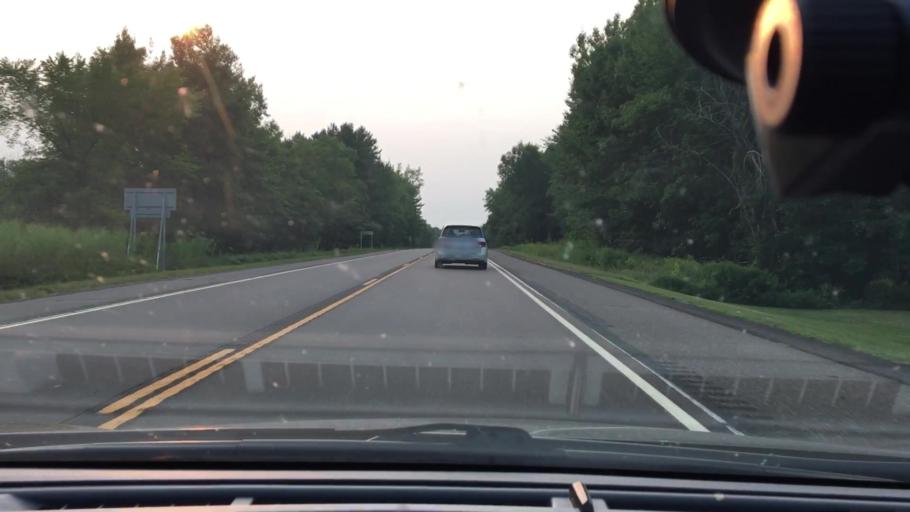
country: US
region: Minnesota
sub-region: Mille Lacs County
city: Vineland
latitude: 46.1465
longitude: -93.7280
